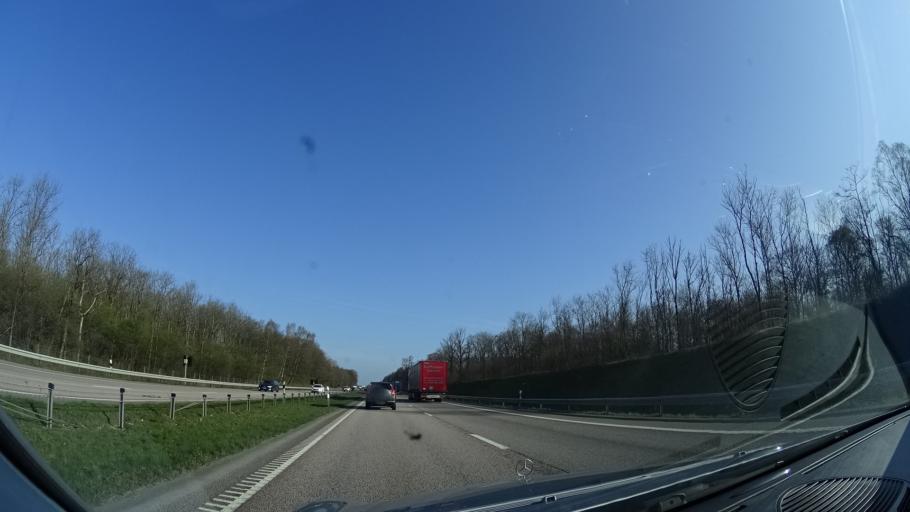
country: SE
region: Skane
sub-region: Helsingborg
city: Barslov
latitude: 56.0560
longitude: 12.7837
